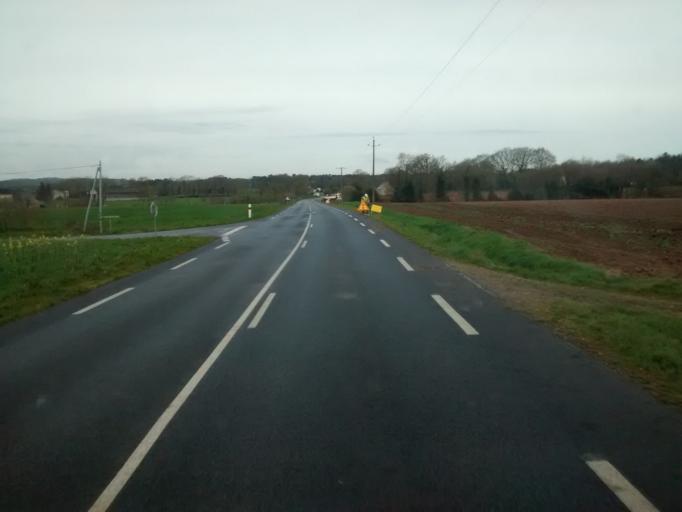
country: FR
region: Brittany
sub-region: Departement du Morbihan
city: Malestroit
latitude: 47.8403
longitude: -2.4088
